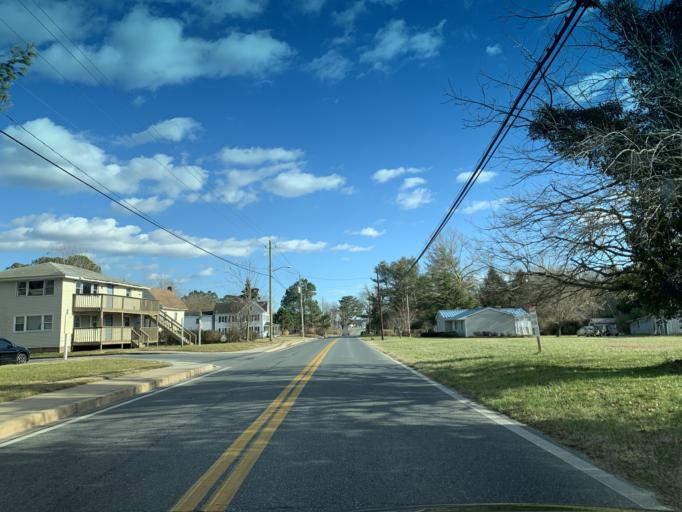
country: US
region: Maryland
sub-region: Worcester County
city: Berlin
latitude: 38.3231
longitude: -75.2076
